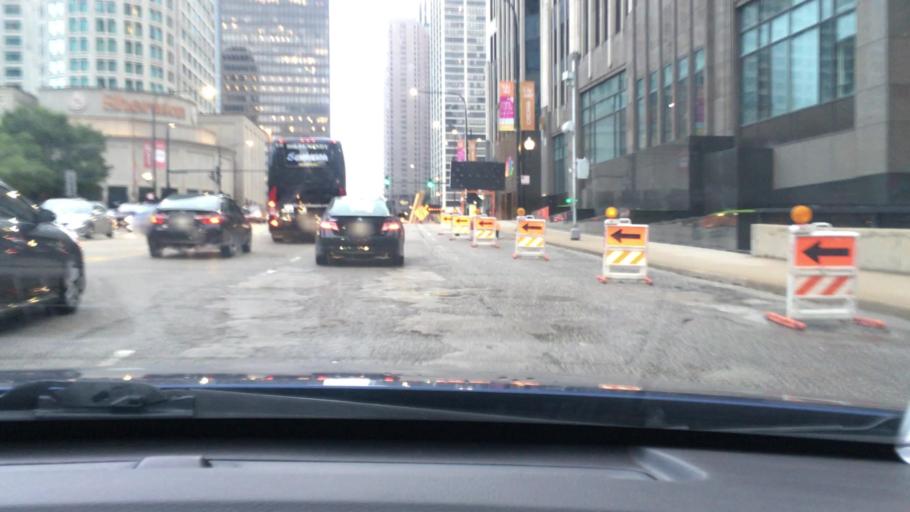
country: US
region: Illinois
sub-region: Cook County
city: Chicago
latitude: 41.8906
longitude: -87.6203
